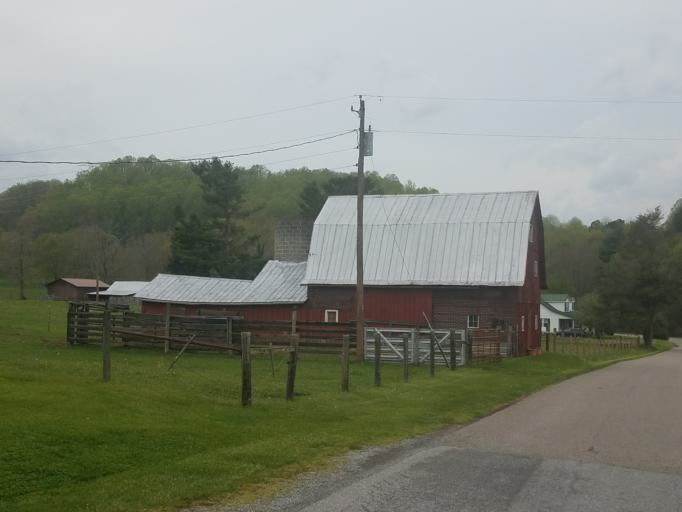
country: US
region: Virginia
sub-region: Smyth County
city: Atkins
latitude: 36.8695
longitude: -81.3619
